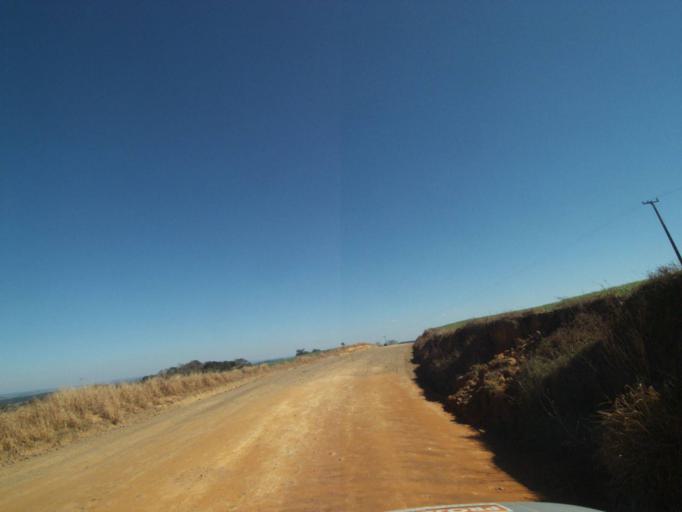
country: BR
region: Parana
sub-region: Tibagi
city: Tibagi
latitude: -24.6189
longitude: -50.6089
